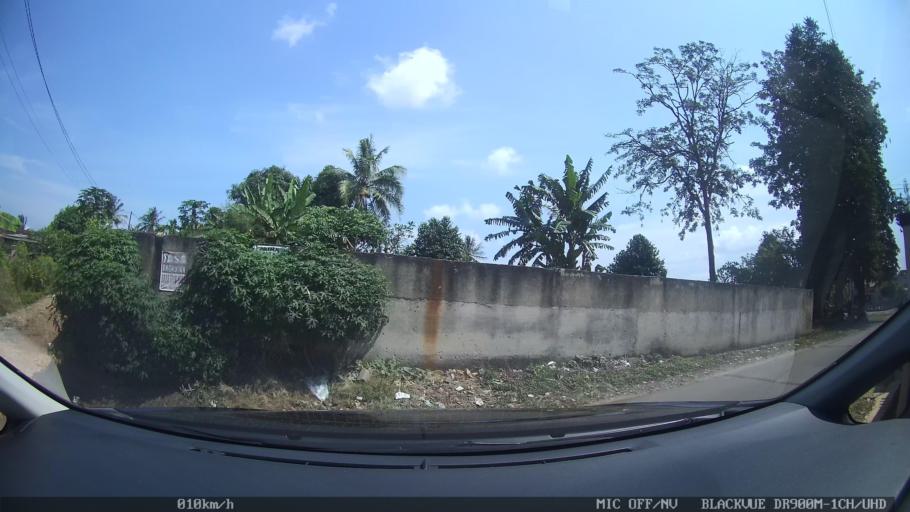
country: ID
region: Lampung
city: Kedaton
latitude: -5.3694
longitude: 105.2504
